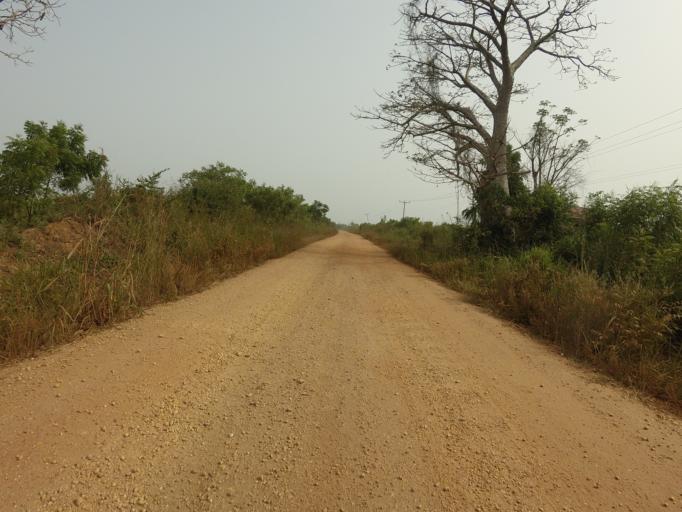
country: GH
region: Volta
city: Anloga
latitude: 5.9767
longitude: 0.6069
